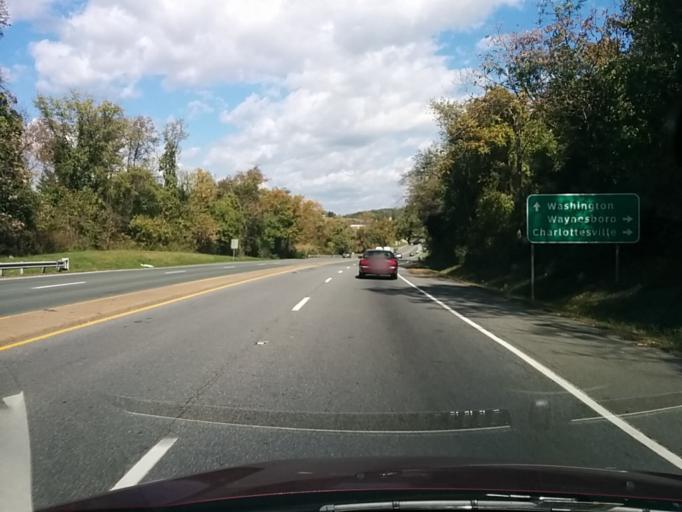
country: US
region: Virginia
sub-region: City of Charlottesville
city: Charlottesville
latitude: 38.0432
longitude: -78.5264
